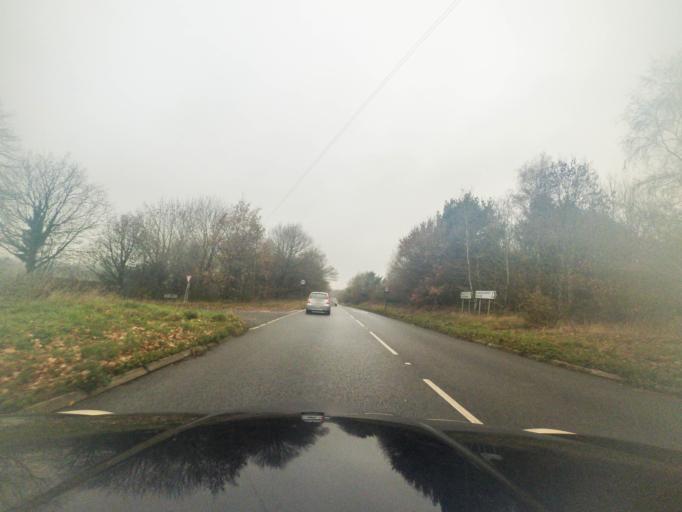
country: GB
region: England
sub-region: Solihull
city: Barston
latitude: 52.3928
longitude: -1.6771
